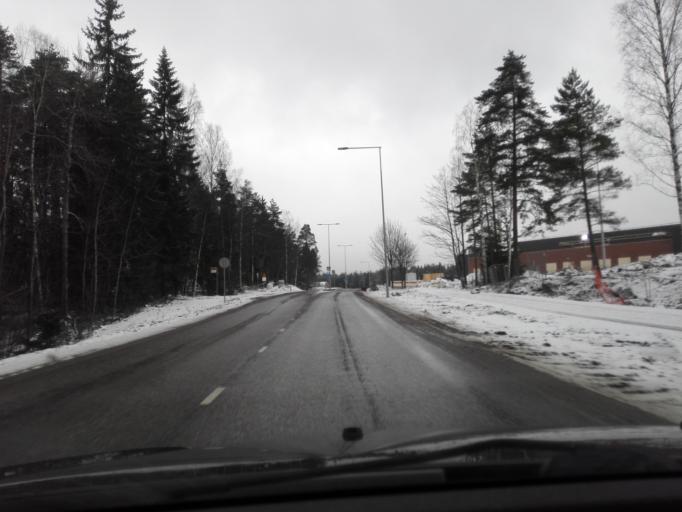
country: FI
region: Uusimaa
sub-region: Helsinki
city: Vantaa
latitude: 60.2867
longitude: 25.0713
